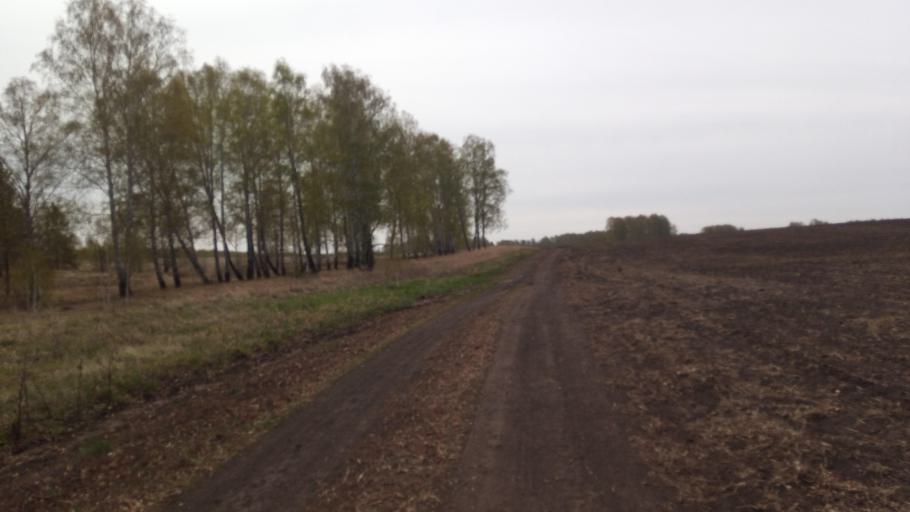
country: RU
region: Chelyabinsk
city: Timiryazevskiy
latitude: 55.0168
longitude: 60.8570
